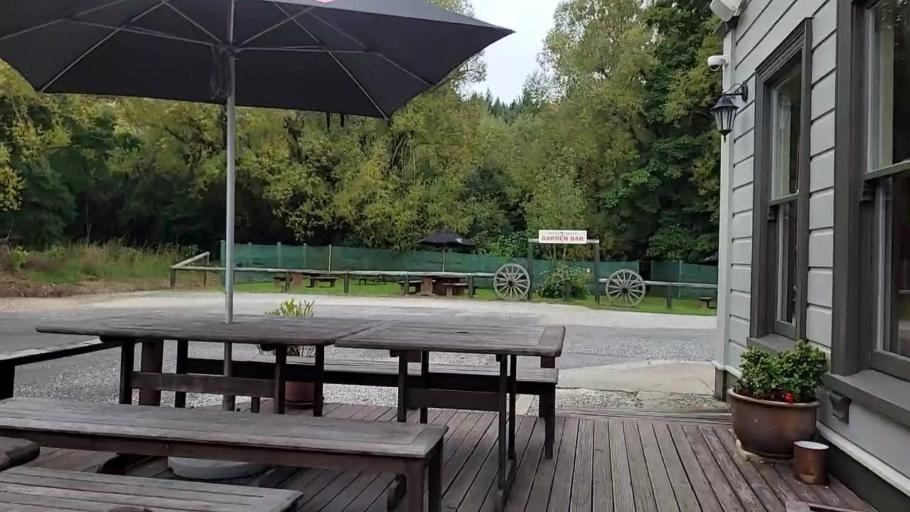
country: NZ
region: Otago
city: Oamaru
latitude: -45.0236
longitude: 170.1477
